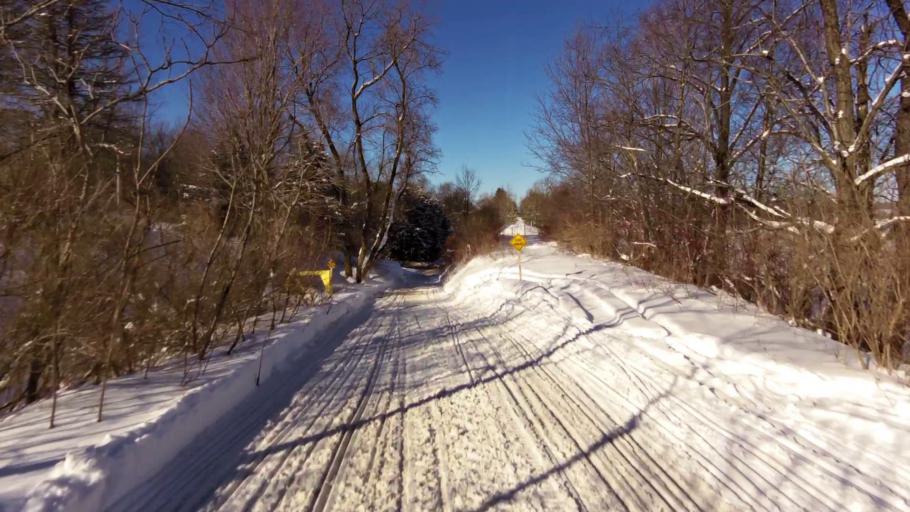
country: US
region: New York
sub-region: Chautauqua County
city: Mayville
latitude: 42.1588
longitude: -79.5861
